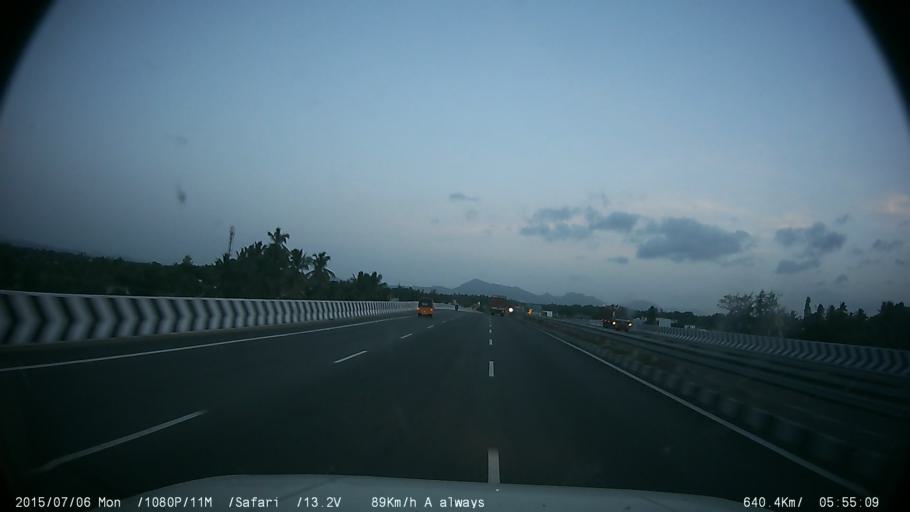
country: IN
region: Tamil Nadu
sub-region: Krishnagiri
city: Krishnagiri
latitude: 12.5599
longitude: 78.1829
